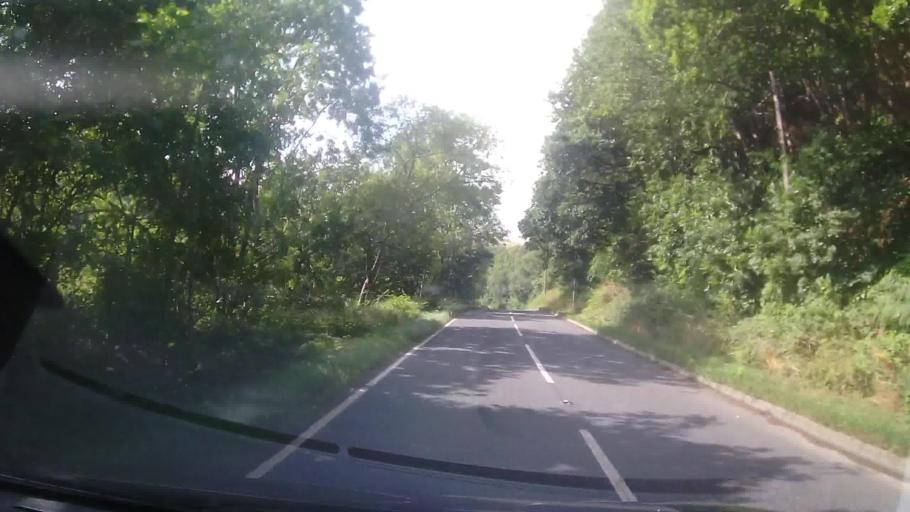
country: GB
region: Wales
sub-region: Sir Powys
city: Knighton
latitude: 52.3581
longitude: -3.0426
